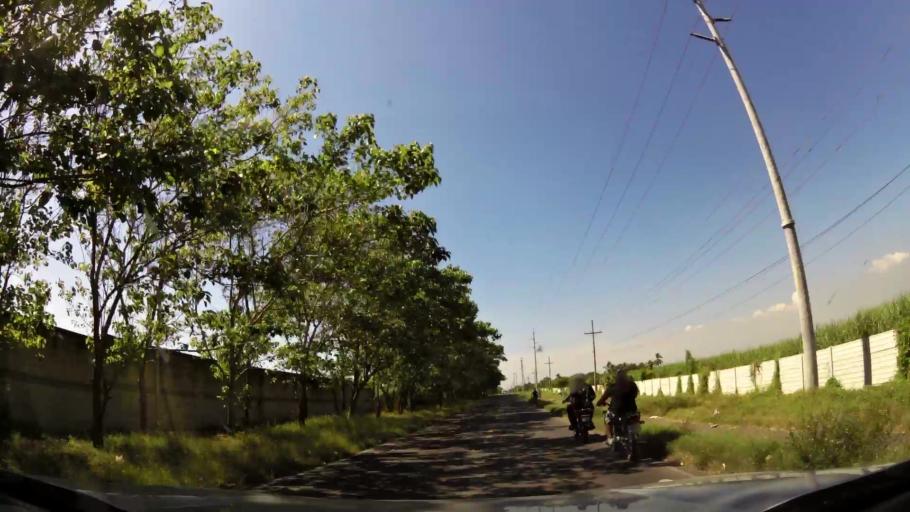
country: GT
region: Escuintla
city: Iztapa
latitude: 13.9345
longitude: -90.7555
